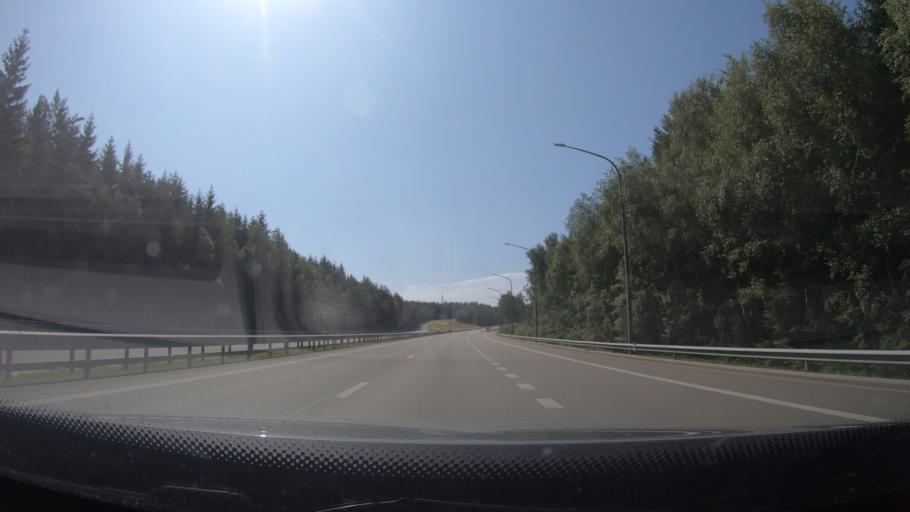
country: BE
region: Wallonia
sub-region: Province de Liege
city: Saint-Vith
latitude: 50.3433
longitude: 6.0850
